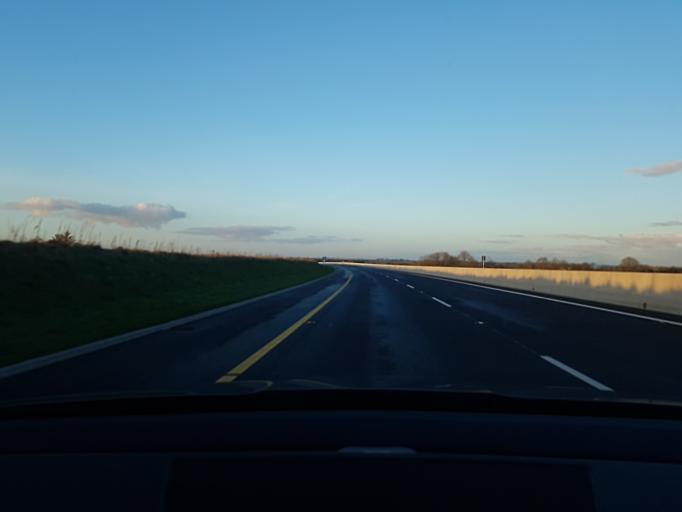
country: IE
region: Connaught
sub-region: County Galway
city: Tuam
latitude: 53.4539
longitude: -8.8475
